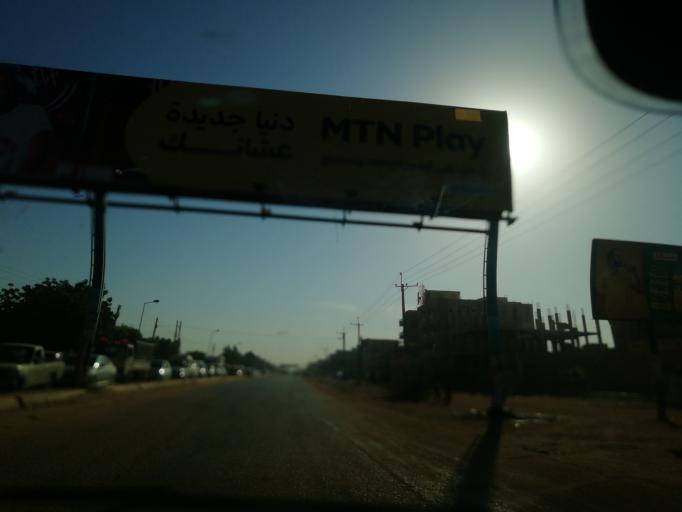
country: SD
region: Khartoum
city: Khartoum
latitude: 15.6103
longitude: 32.6203
